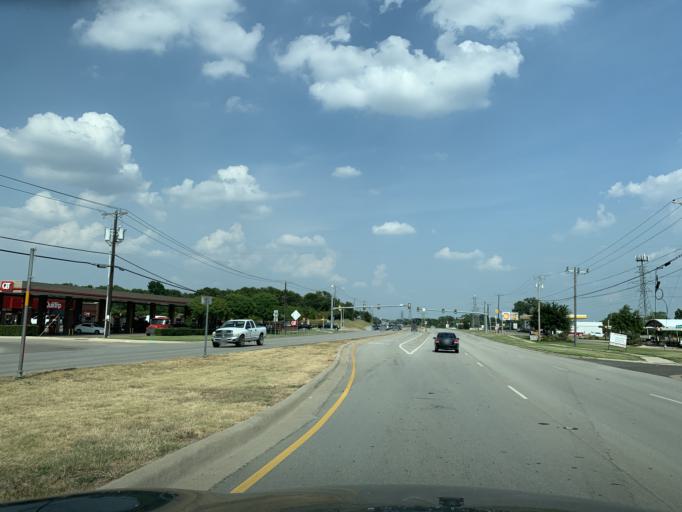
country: US
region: Texas
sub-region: Tarrant County
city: Richland Hills
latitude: 32.8089
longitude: -97.2080
